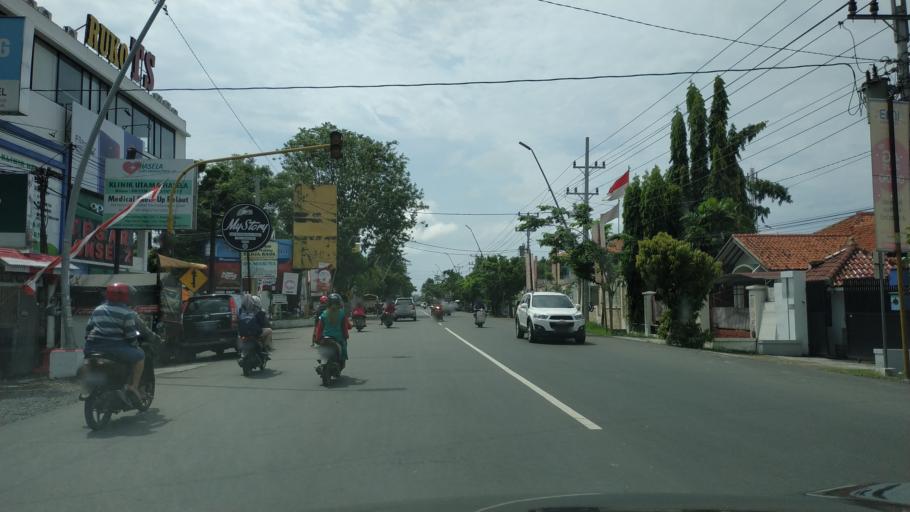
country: ID
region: Central Java
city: Tegal
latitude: -6.8756
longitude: 109.1273
